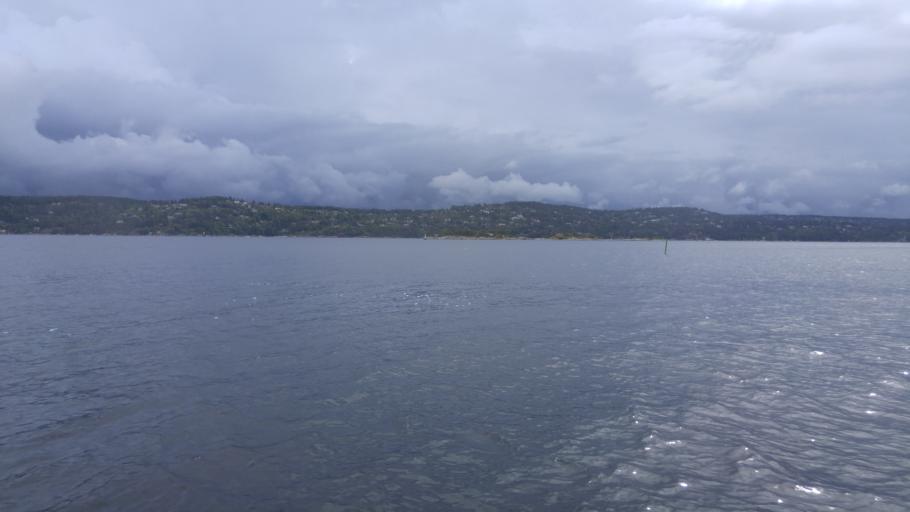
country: NO
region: Akershus
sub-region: Nesodden
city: Fagerstrand
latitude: 59.7040
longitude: 10.5697
